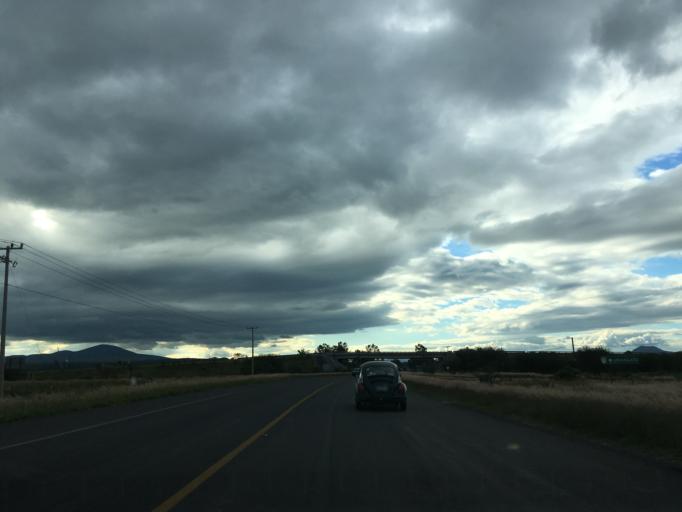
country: MX
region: Michoacan
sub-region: Cuitzeo
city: Cuamio
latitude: 20.0767
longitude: -101.1344
